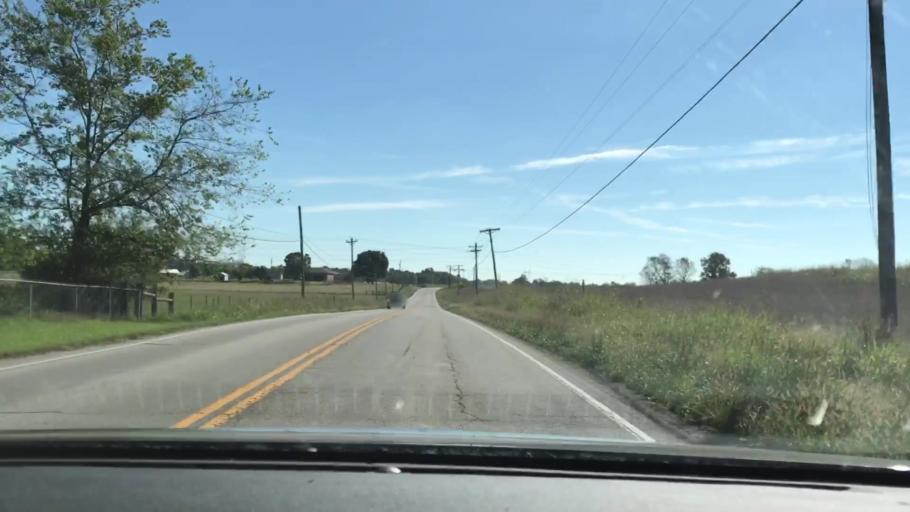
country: US
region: Kentucky
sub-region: Christian County
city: Hopkinsville
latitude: 36.8613
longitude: -87.4375
